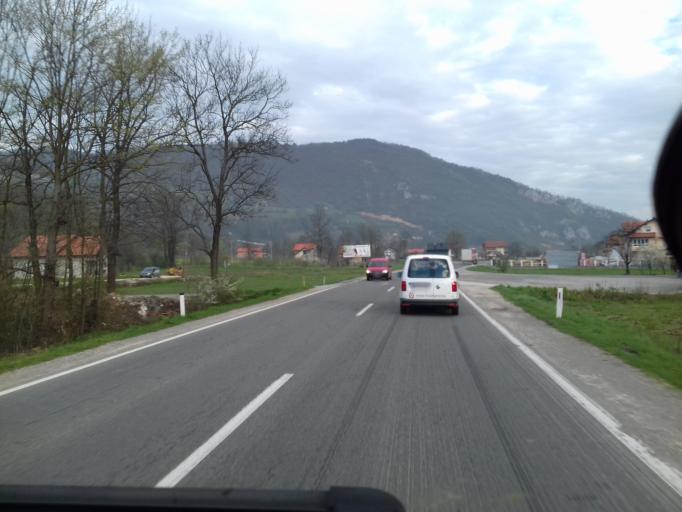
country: BA
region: Federation of Bosnia and Herzegovina
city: Maglaj
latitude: 44.6220
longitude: 18.0966
